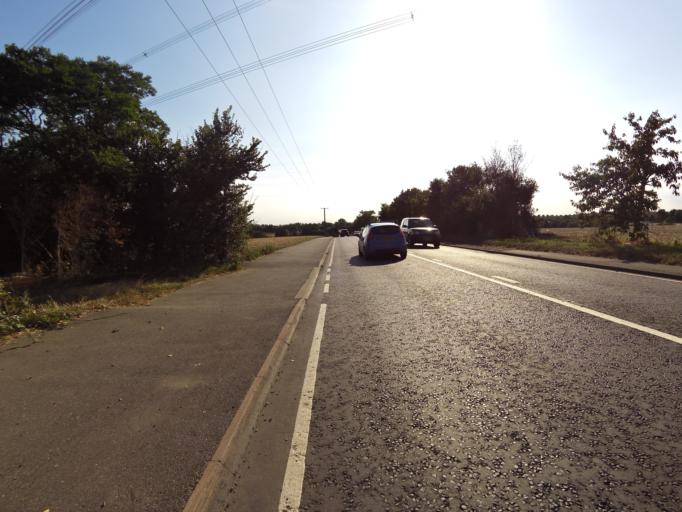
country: GB
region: England
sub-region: Essex
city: Hatfield Peverel
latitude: 51.7596
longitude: 0.5339
